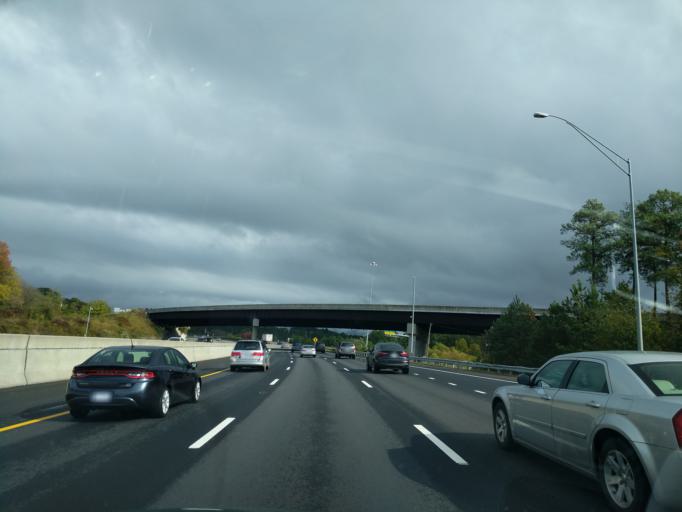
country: US
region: North Carolina
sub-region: Durham County
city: Durham
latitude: 36.0245
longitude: -78.9503
